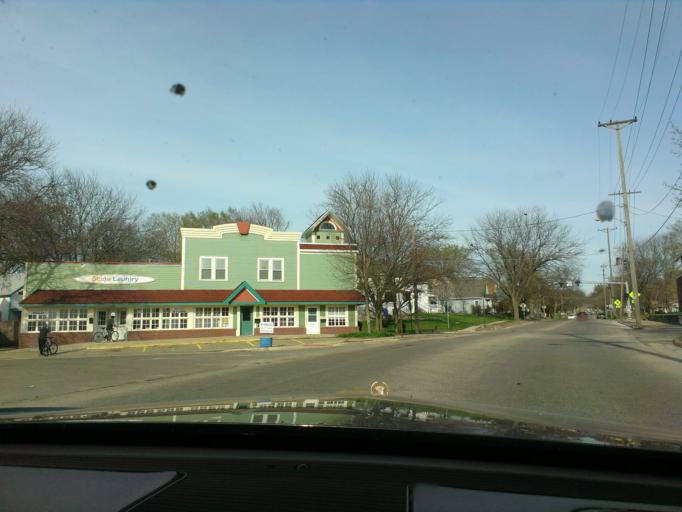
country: US
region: Iowa
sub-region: Linn County
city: Cedar Rapids
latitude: 41.9738
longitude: -91.6517
